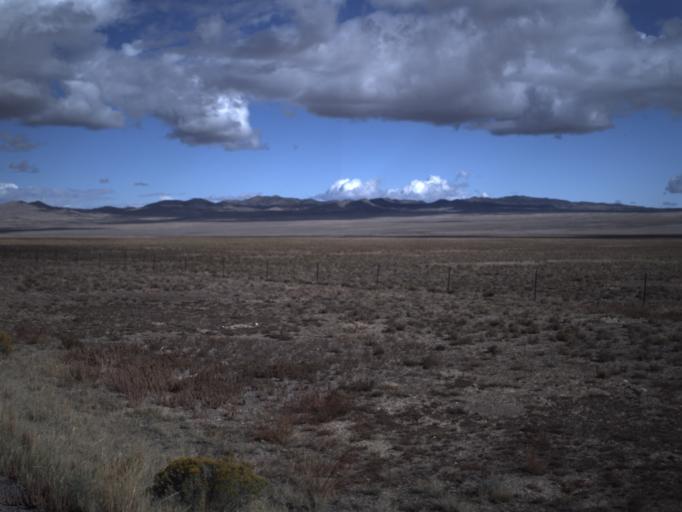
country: US
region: Utah
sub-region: Beaver County
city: Milford
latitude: 38.6605
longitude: -113.8768
